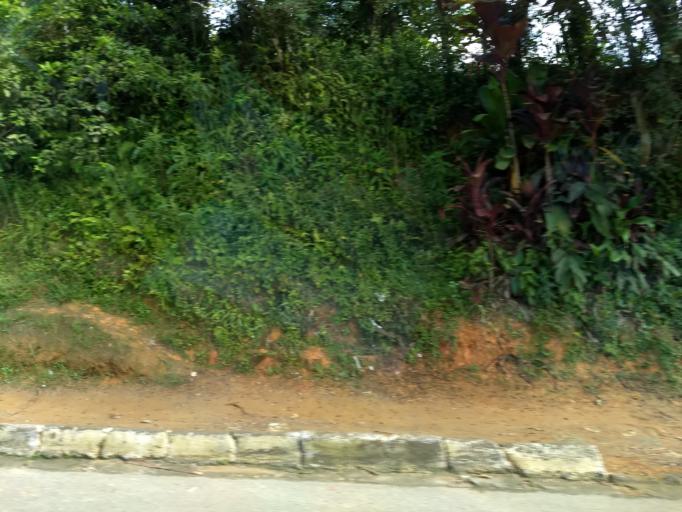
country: BR
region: Santa Catarina
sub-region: Schroeder
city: Schroeder
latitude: -26.4381
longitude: -49.1483
